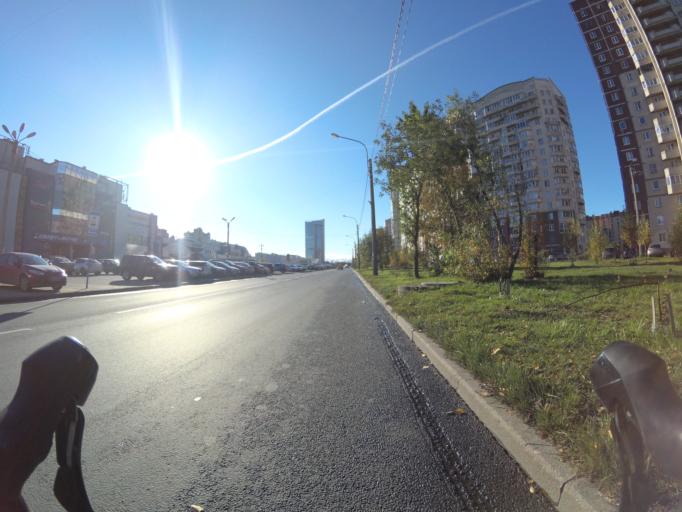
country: RU
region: Leningrad
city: Untolovo
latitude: 59.9917
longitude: 30.2042
